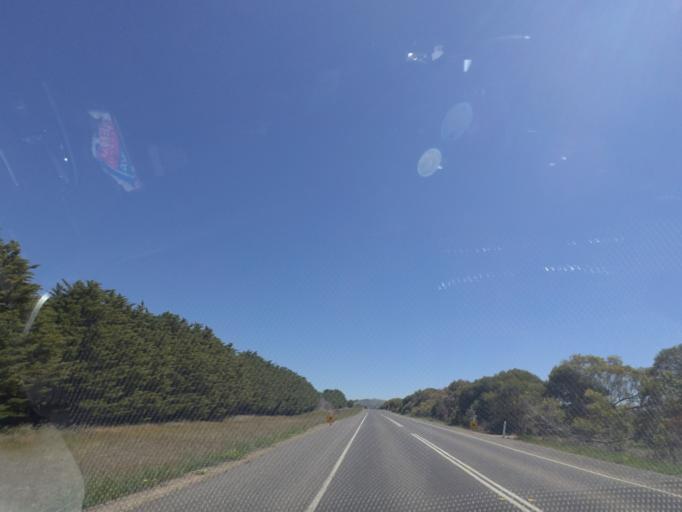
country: AU
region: Victoria
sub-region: Hume
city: Sunbury
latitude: -37.3098
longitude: 144.8440
